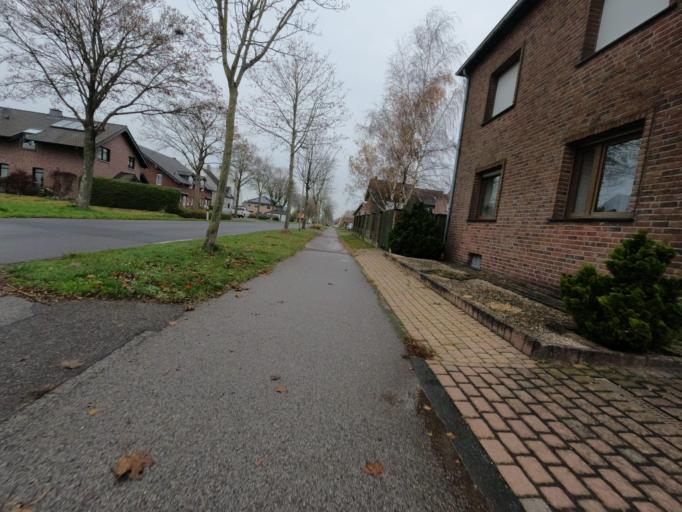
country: DE
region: North Rhine-Westphalia
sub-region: Regierungsbezirk Koln
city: Heinsberg
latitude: 51.0372
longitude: 6.1046
